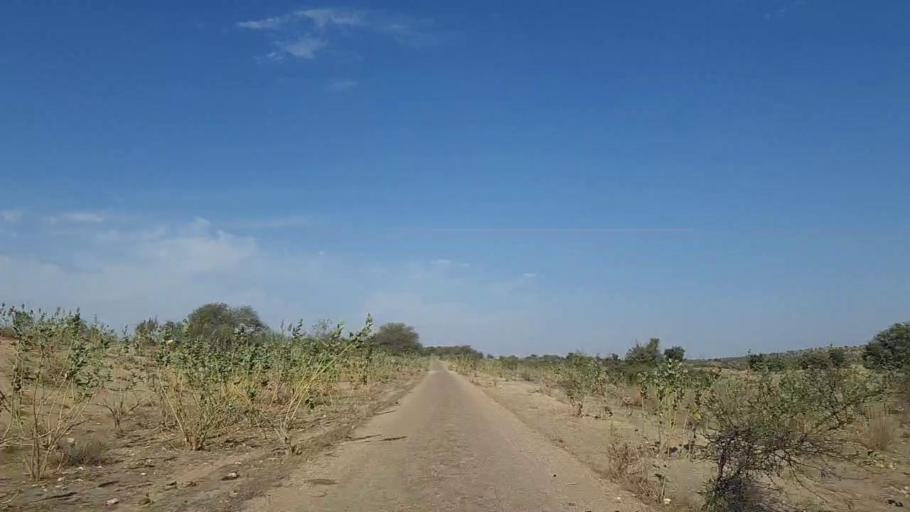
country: PK
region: Sindh
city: Naukot
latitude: 24.8359
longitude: 69.5486
